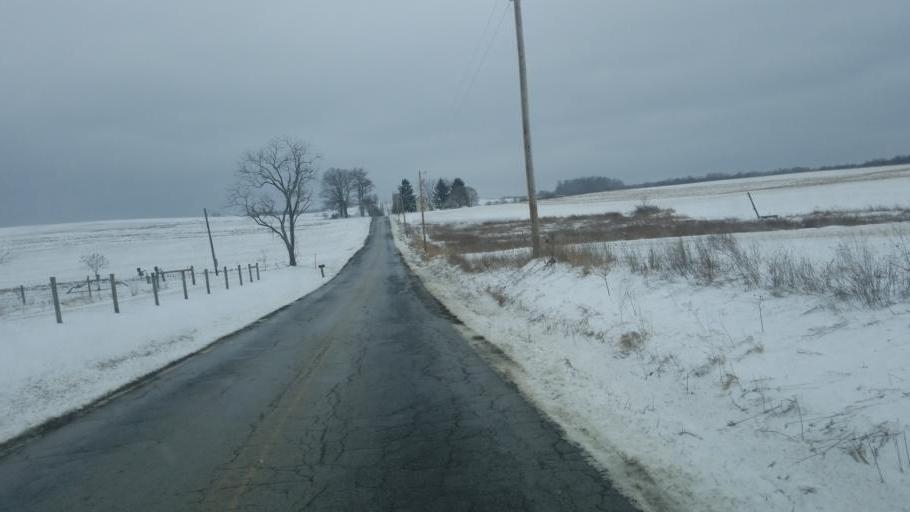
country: US
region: Ohio
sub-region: Knox County
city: Oak Hill
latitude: 40.4847
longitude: -82.1284
